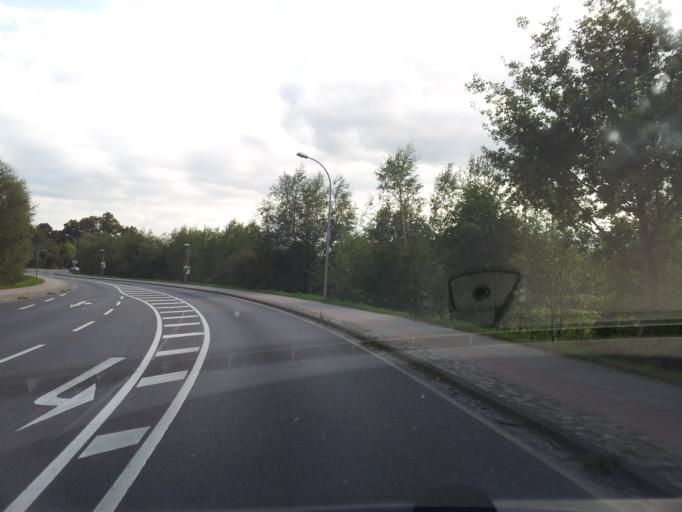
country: DE
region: Brandenburg
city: Ruhland
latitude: 51.4647
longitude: 13.8680
